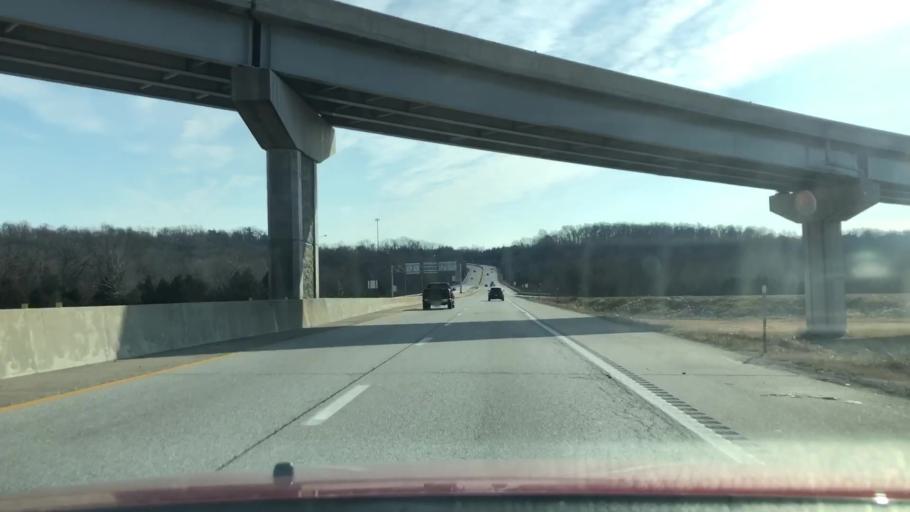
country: US
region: Missouri
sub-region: Christian County
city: Nixa
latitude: 37.1272
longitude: -93.2299
